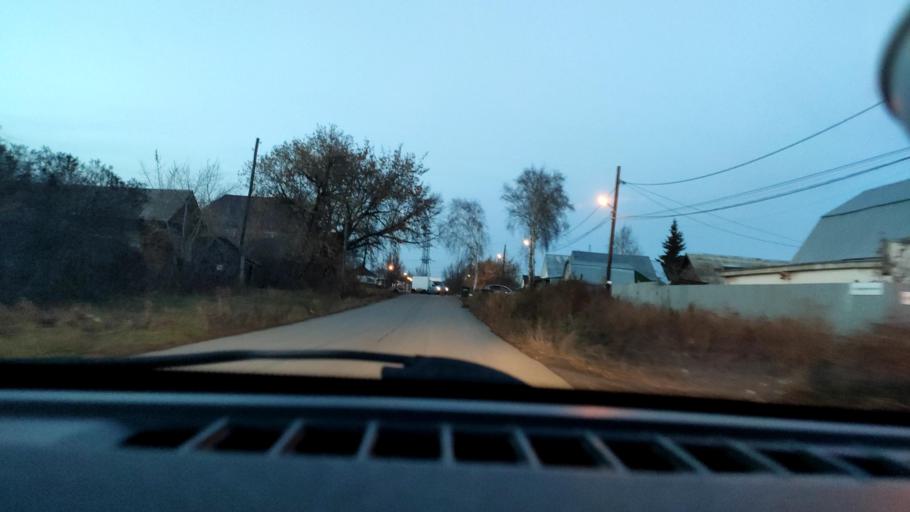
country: RU
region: Samara
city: Petra-Dubrava
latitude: 53.2615
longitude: 50.3299
